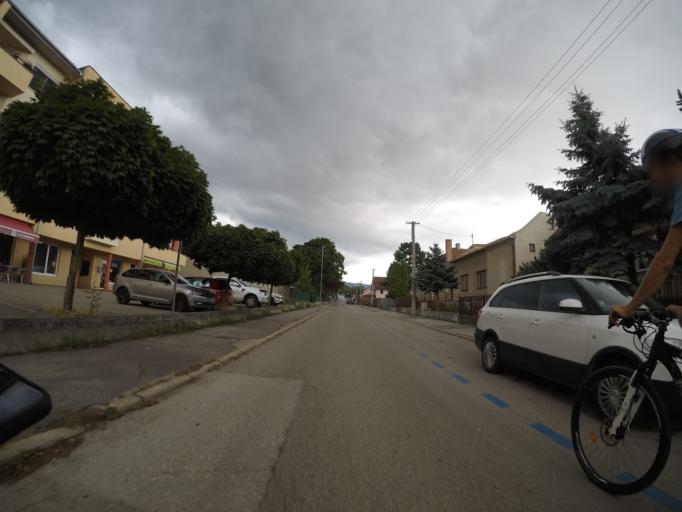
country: SK
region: Trenciansky
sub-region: Okres Trencin
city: Trencin
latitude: 48.8768
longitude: 18.0320
